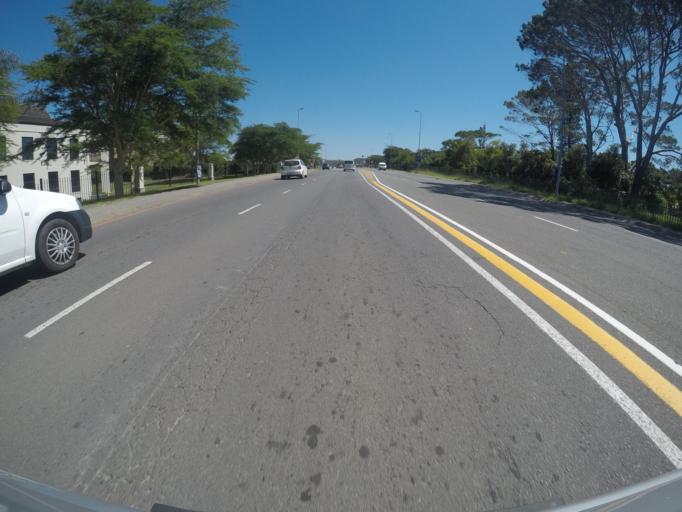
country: ZA
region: Eastern Cape
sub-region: Buffalo City Metropolitan Municipality
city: East London
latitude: -32.9561
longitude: 27.9344
